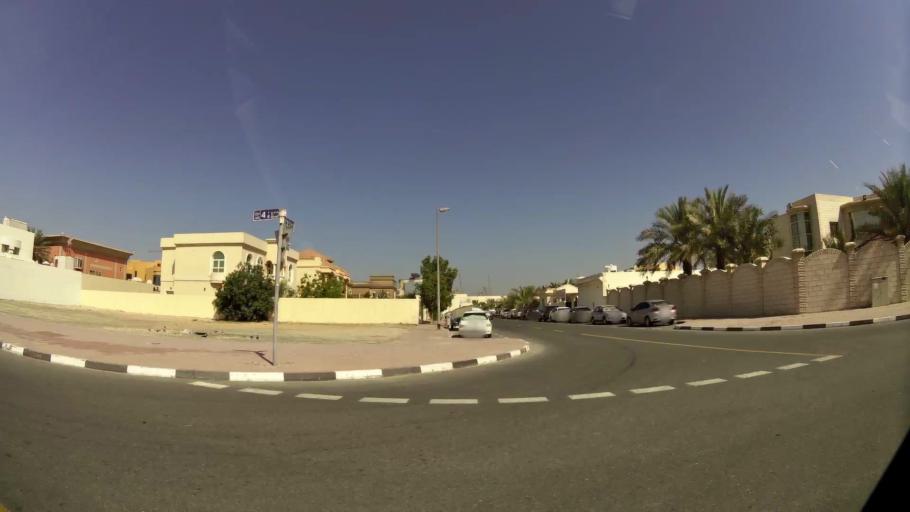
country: AE
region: Ash Shariqah
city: Sharjah
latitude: 25.2467
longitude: 55.2819
